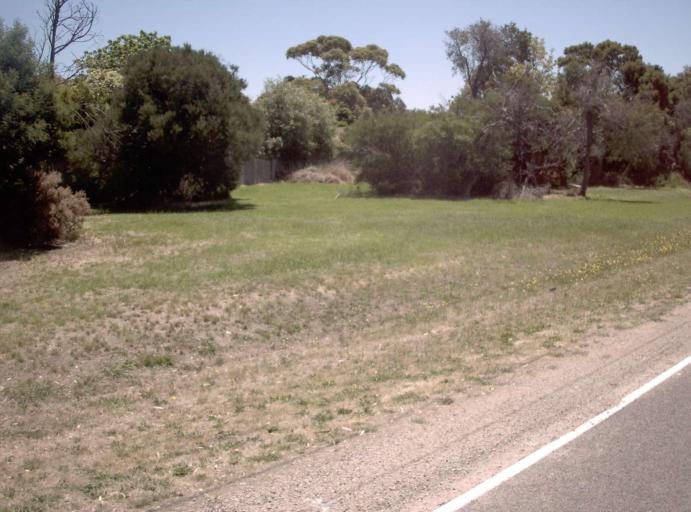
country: AU
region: Victoria
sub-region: Mornington Peninsula
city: Mount Martha
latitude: -38.2499
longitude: 145.0367
